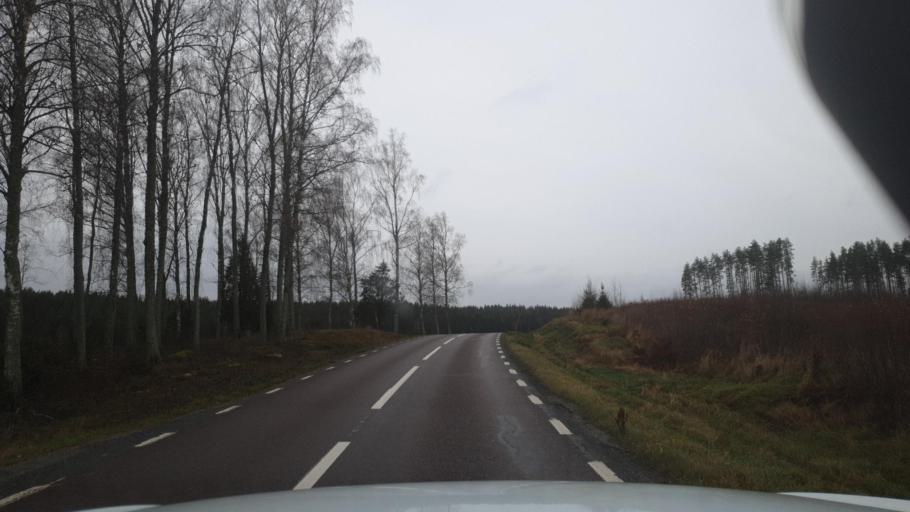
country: SE
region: Vaermland
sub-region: Arvika Kommun
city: Arvika
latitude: 59.5897
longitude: 12.5405
